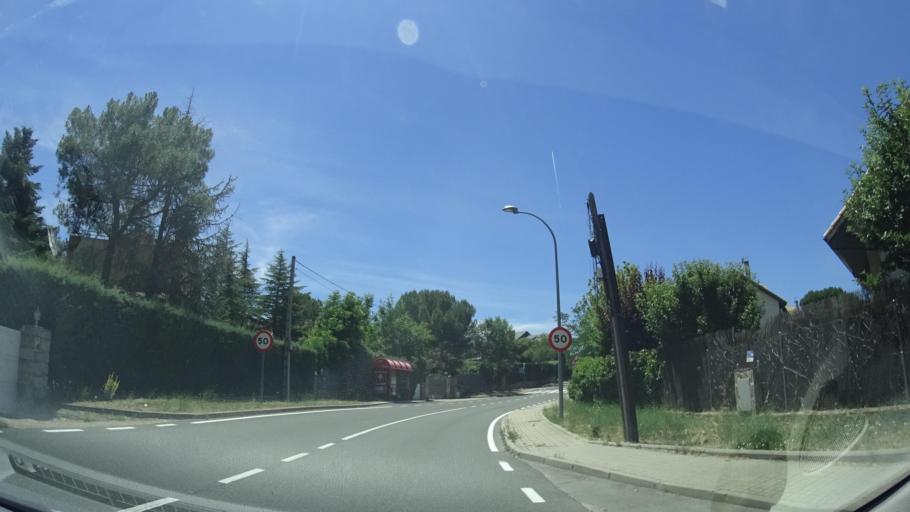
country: ES
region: Madrid
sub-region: Provincia de Madrid
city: Galapagar
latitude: 40.6034
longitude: -3.9830
